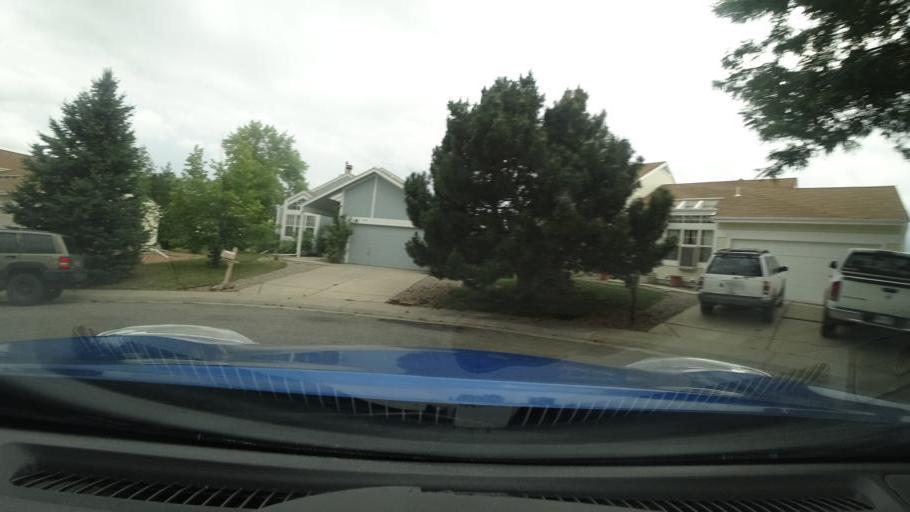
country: US
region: Colorado
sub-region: Adams County
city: Aurora
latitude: 39.7018
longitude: -104.8135
